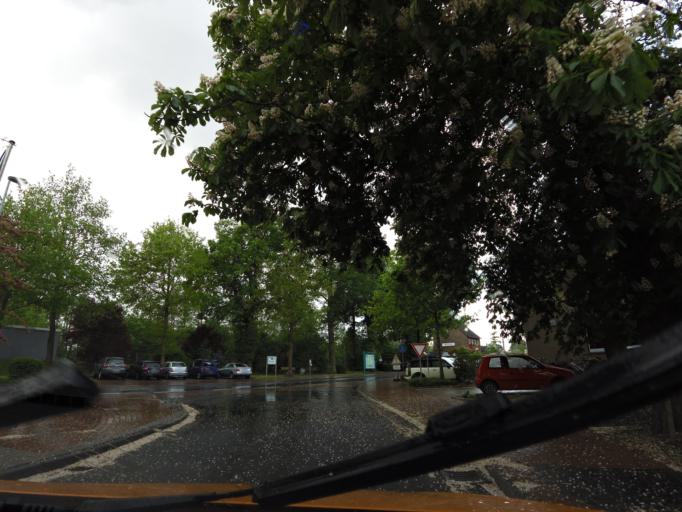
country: DE
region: Lower Saxony
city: Hatten
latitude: 53.1187
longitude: 8.3363
